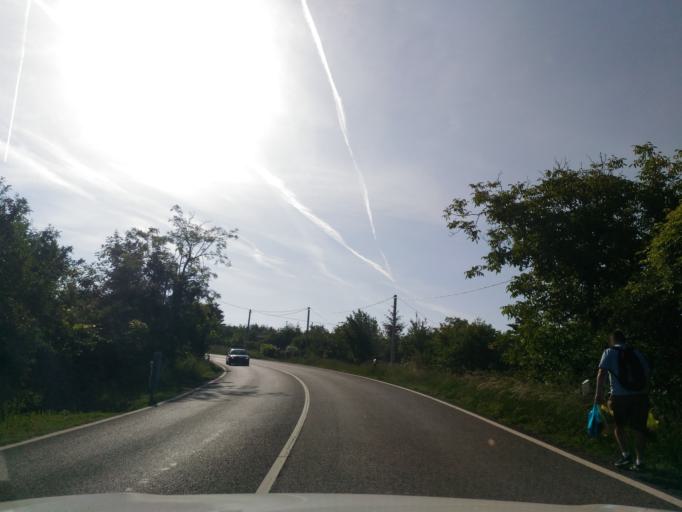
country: HU
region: Baranya
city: Komlo
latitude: 46.1759
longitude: 18.2615
